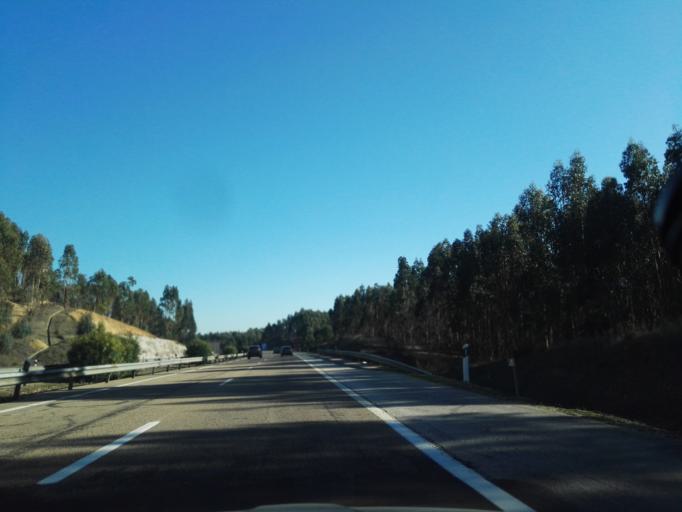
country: PT
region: Santarem
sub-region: Chamusca
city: Vila Nova da Barquinha
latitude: 39.4866
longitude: -8.4185
